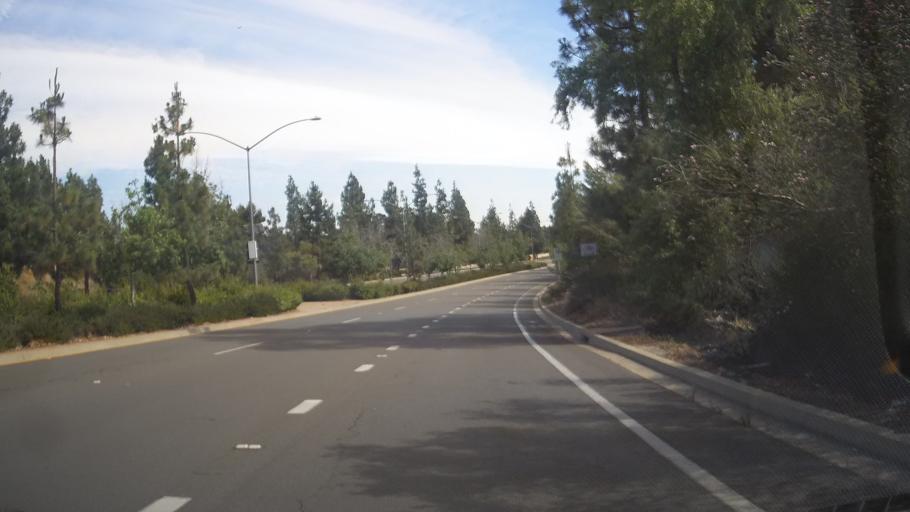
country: US
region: California
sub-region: San Diego County
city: La Mesa
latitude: 32.7896
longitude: -117.0021
